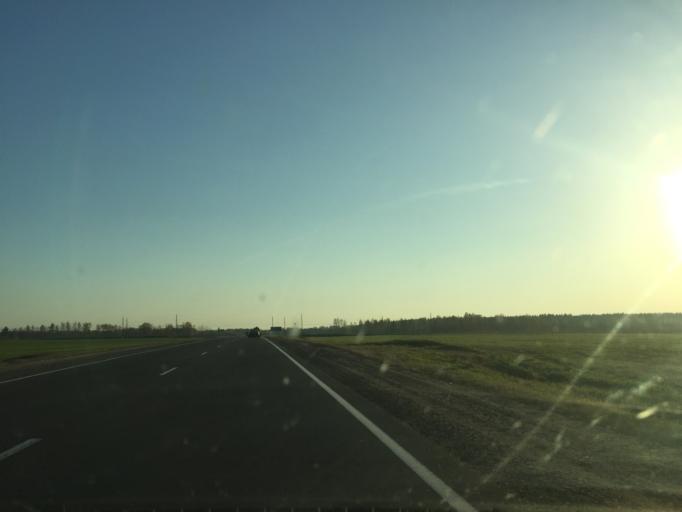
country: BY
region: Mogilev
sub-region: Mahilyowski Rayon
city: Kadino
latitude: 53.8718
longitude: 30.4849
